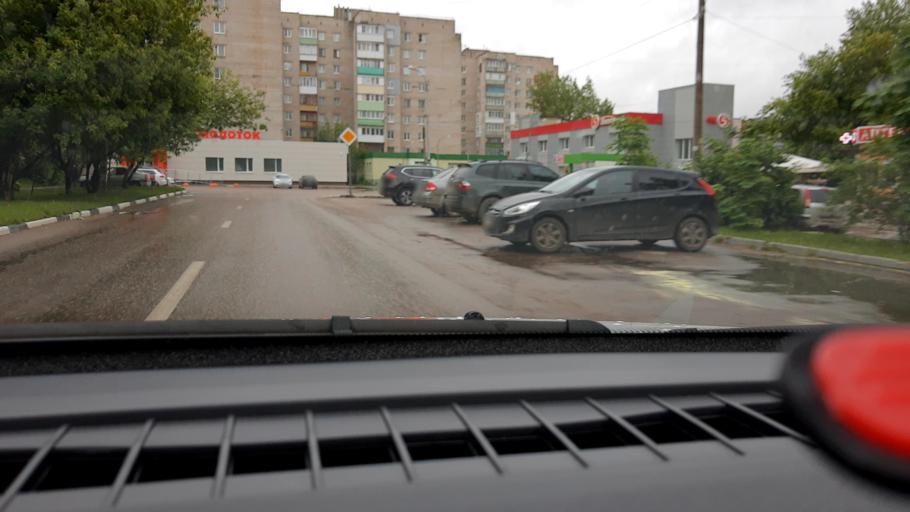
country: RU
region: Nizjnij Novgorod
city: Bor
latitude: 56.3540
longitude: 44.0699
